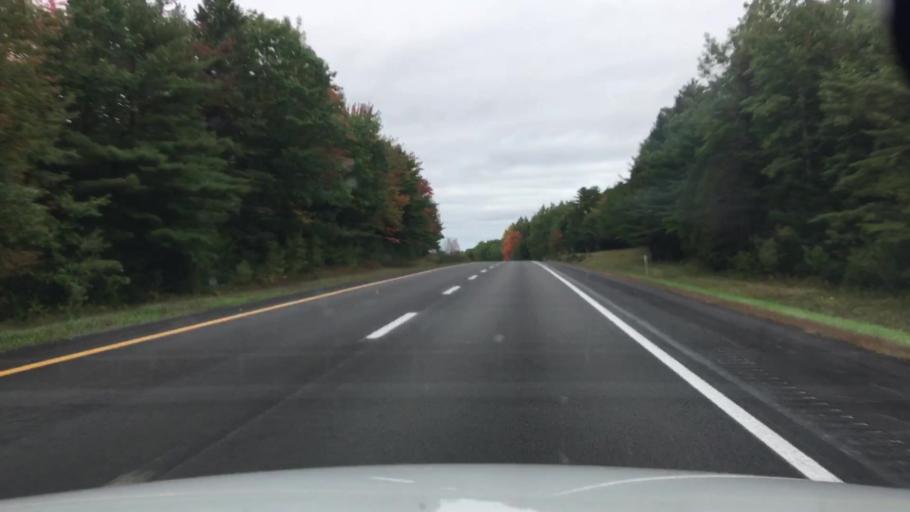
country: US
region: Maine
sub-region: Penobscot County
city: Orono
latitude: 44.8917
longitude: -68.6921
